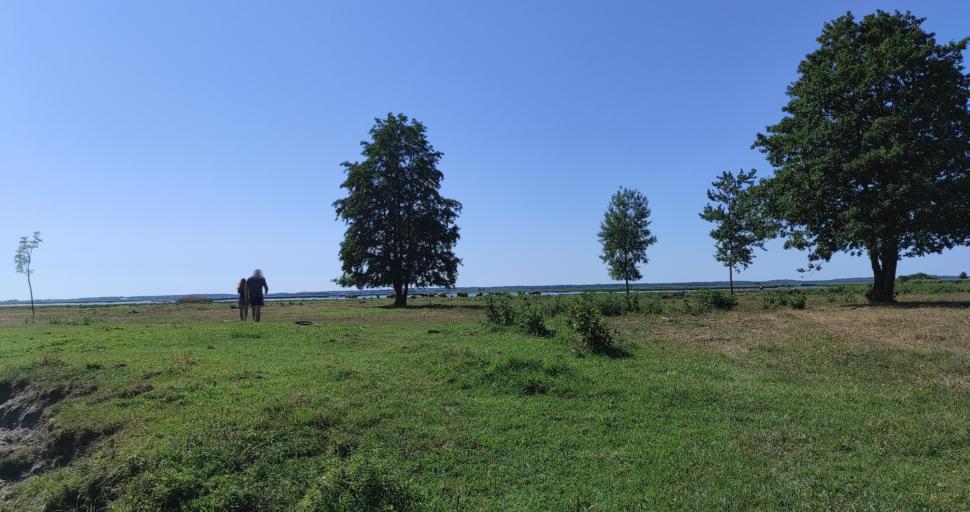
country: LV
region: Rucavas
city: Rucava
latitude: 56.1937
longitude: 21.0744
